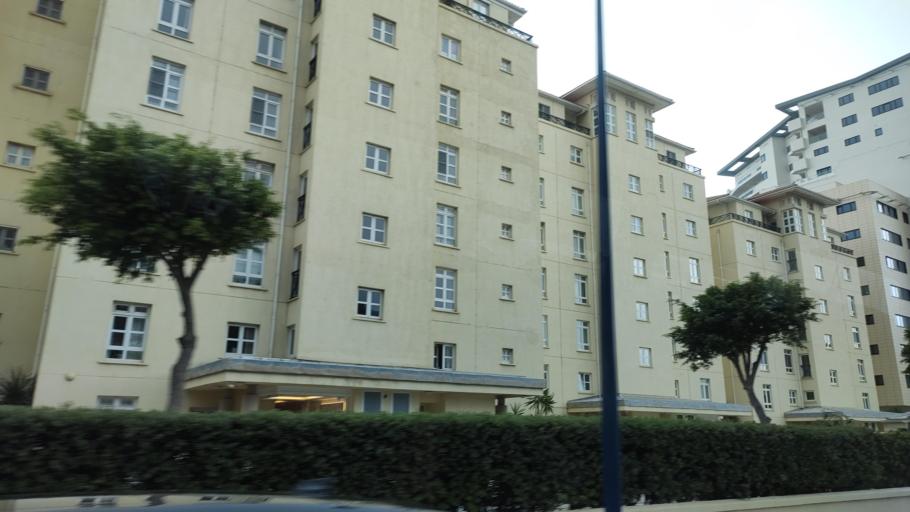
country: GI
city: Gibraltar
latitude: 36.1365
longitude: -5.3548
